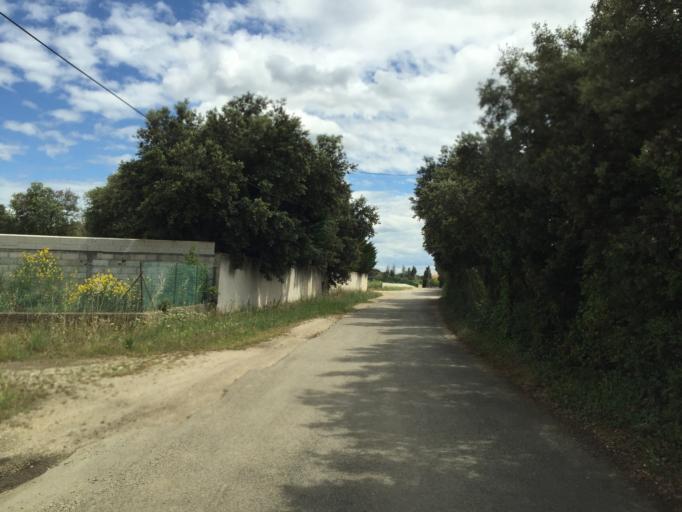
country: FR
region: Provence-Alpes-Cote d'Azur
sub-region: Departement du Vaucluse
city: Sorgues
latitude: 44.0262
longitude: 4.8529
